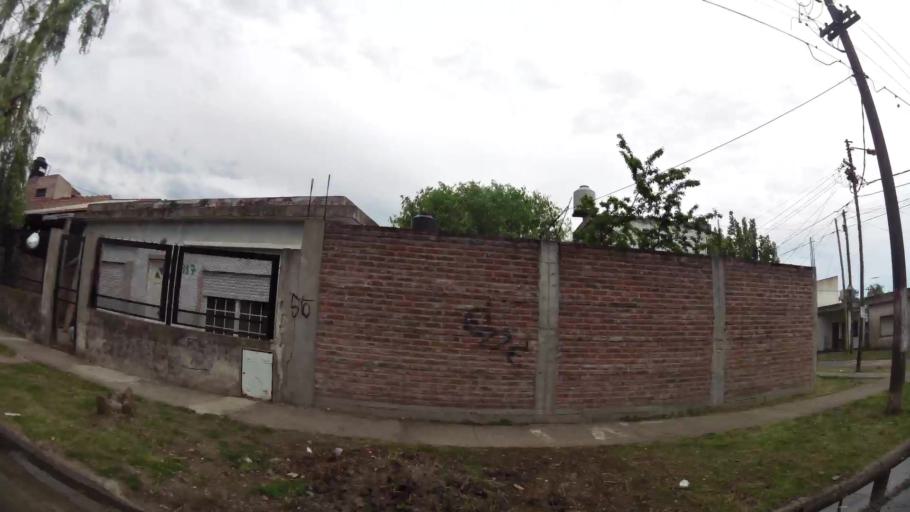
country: AR
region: Buenos Aires
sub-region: Partido de Quilmes
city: Quilmes
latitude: -34.7621
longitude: -58.1967
